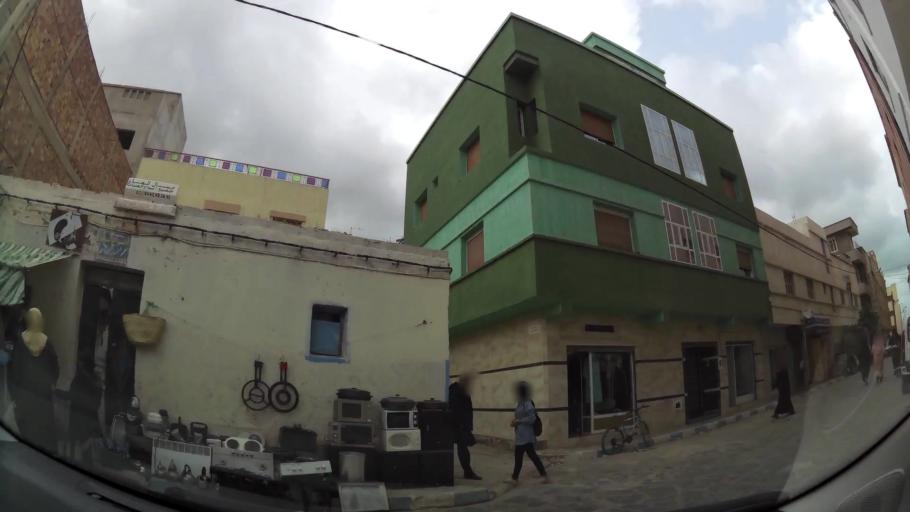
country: MA
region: Oriental
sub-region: Nador
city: Nador
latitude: 35.1709
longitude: -2.9377
